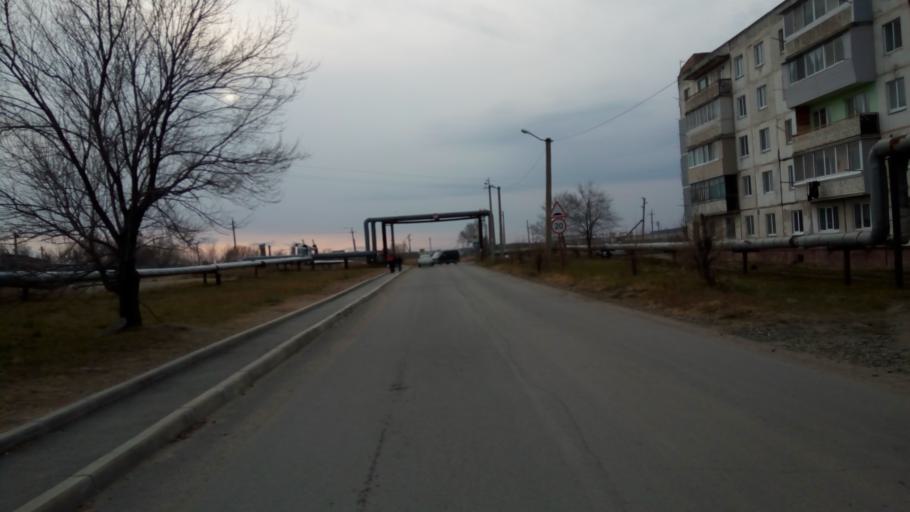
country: RU
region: Primorskiy
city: Novoshakhtinskiy
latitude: 44.0242
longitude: 132.1685
